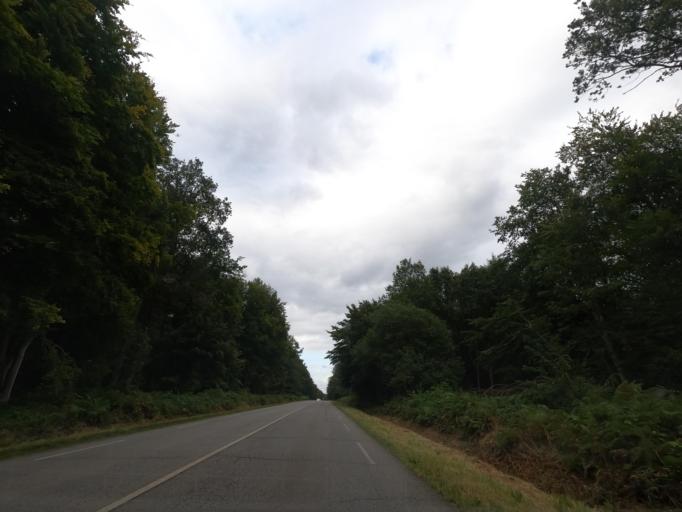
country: FR
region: Haute-Normandie
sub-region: Departement de l'Eure
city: Bourgtheroulde-Infreville
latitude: 49.3237
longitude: 0.9057
